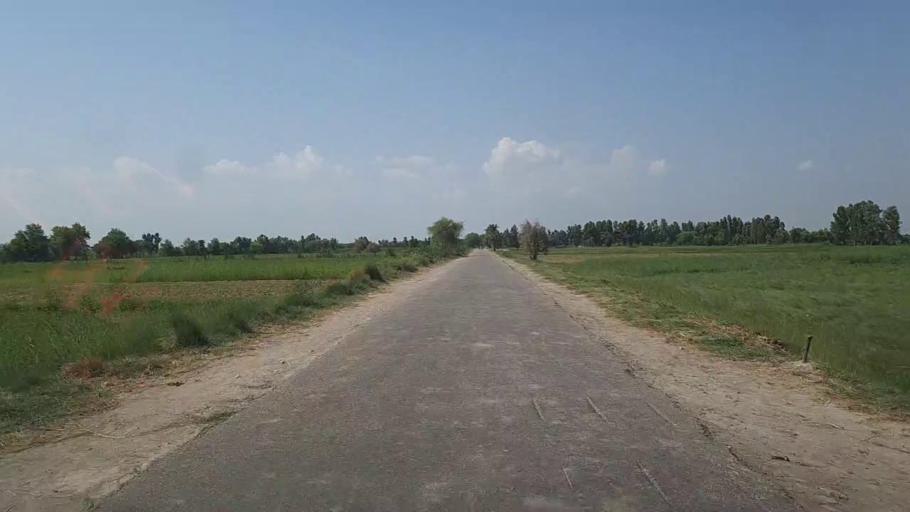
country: PK
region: Sindh
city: Khairpur
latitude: 28.0790
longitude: 69.6372
